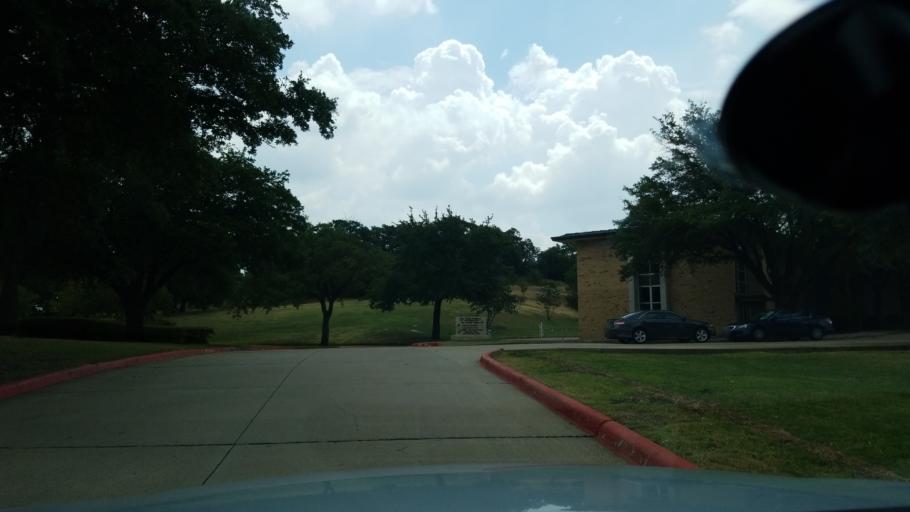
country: US
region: Texas
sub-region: Dallas County
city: Irving
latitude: 32.8504
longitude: -96.9228
